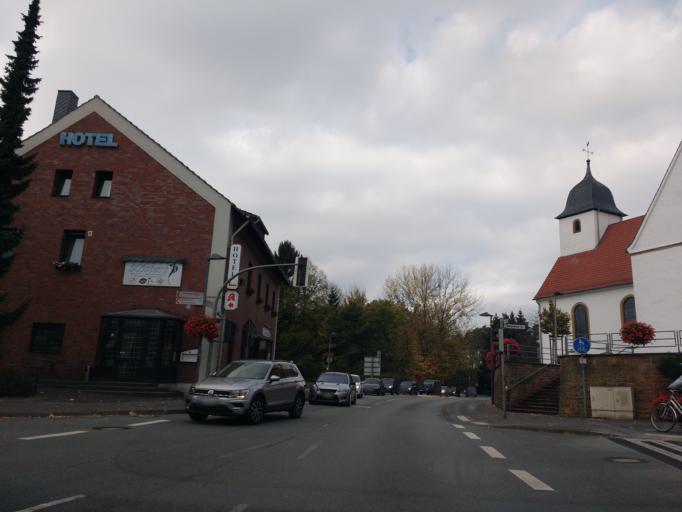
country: DE
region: North Rhine-Westphalia
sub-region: Regierungsbezirk Detmold
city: Oerlinghausen
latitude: 51.9121
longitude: 8.6565
